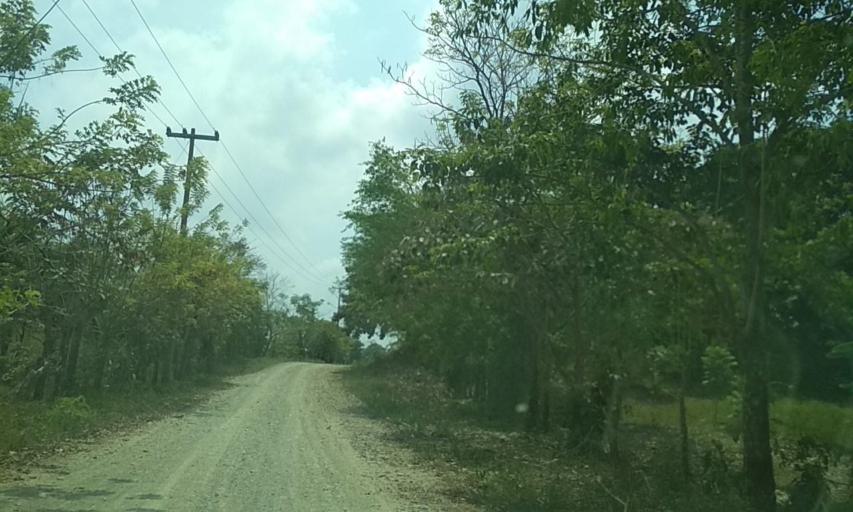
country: MX
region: Tabasco
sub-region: Huimanguillo
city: Francisco Rueda
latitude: 17.6284
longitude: -93.8204
